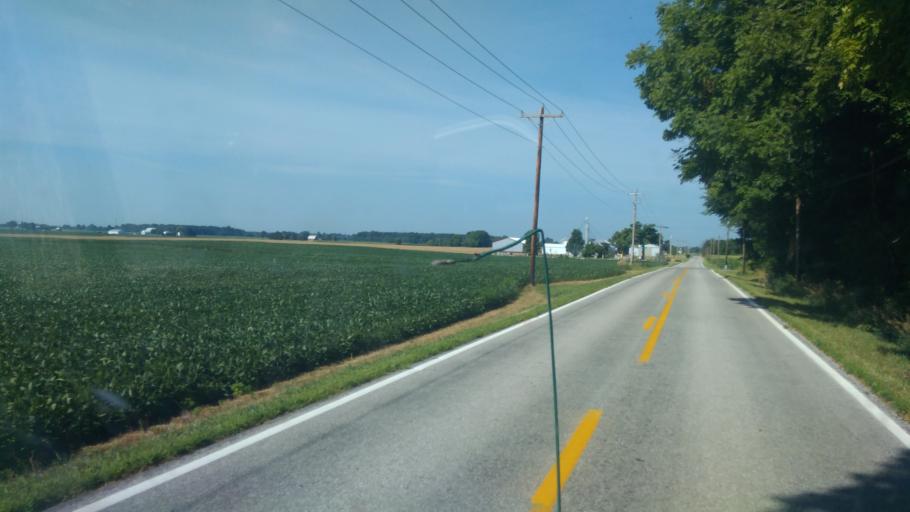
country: US
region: Ohio
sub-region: Delaware County
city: Delaware
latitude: 40.3018
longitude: -83.1837
